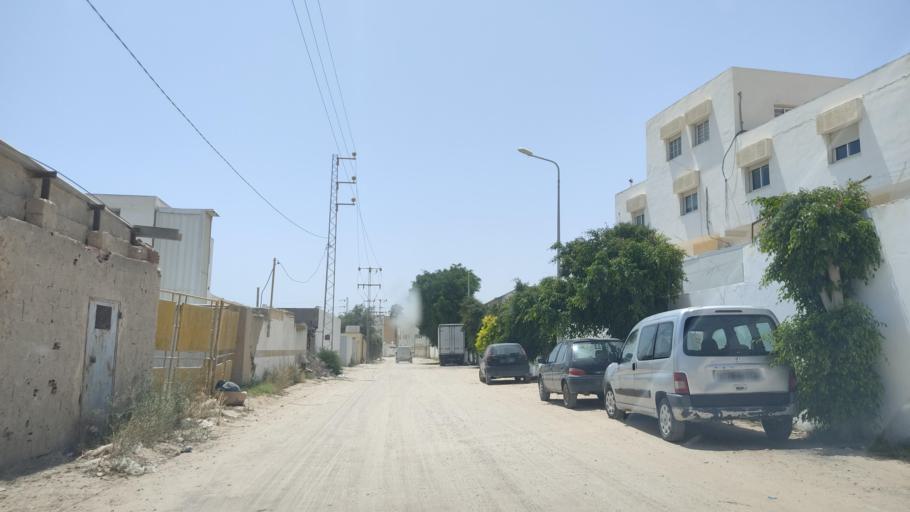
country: TN
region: Safaqis
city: Sfax
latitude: 34.7103
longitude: 10.7288
